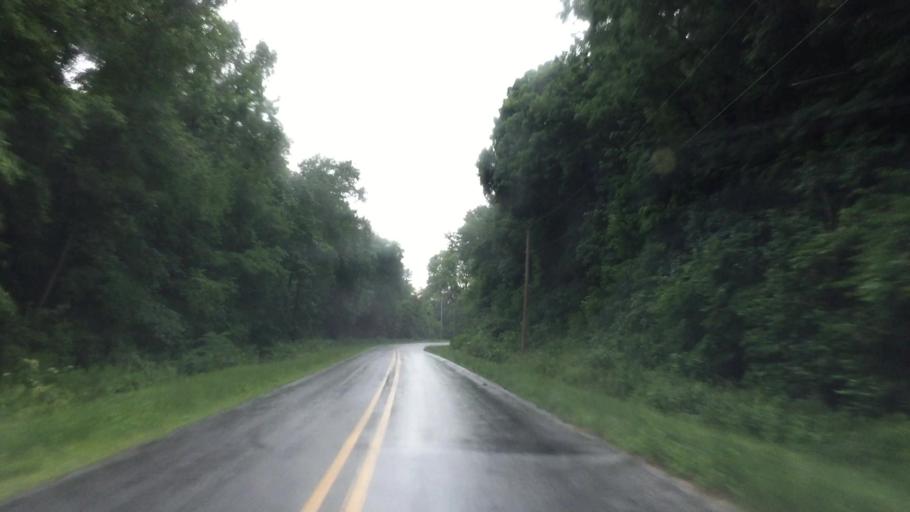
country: US
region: Iowa
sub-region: Lee County
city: Fort Madison
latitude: 40.6101
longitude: -91.2808
